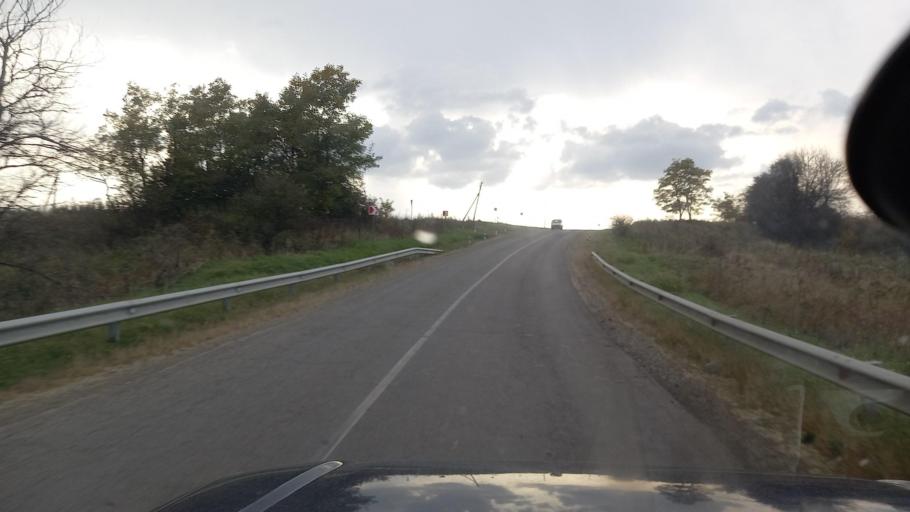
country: RU
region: Krasnodarskiy
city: Gubskaya
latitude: 44.3508
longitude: 40.6962
